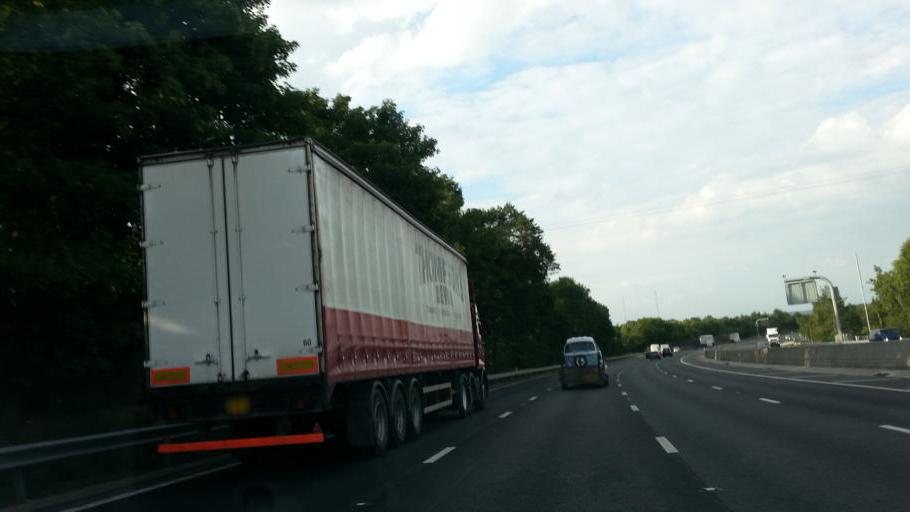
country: GB
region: England
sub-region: Worcestershire
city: Droitwich
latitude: 52.2650
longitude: -2.1363
